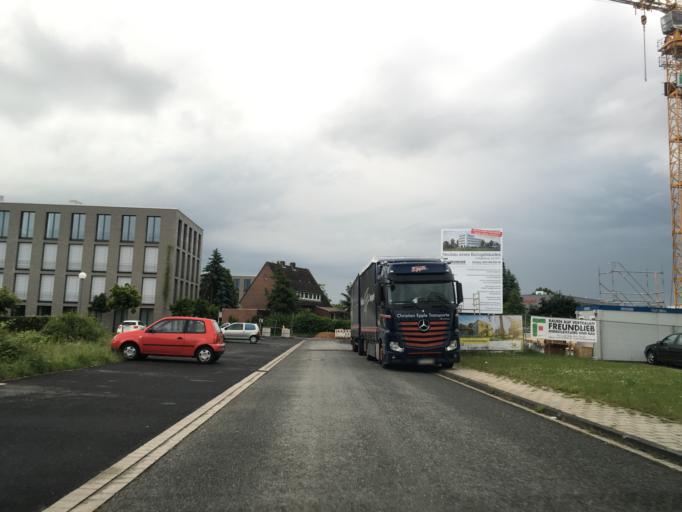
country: DE
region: North Rhine-Westphalia
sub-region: Regierungsbezirk Munster
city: Muenster
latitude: 51.9774
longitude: 7.5970
